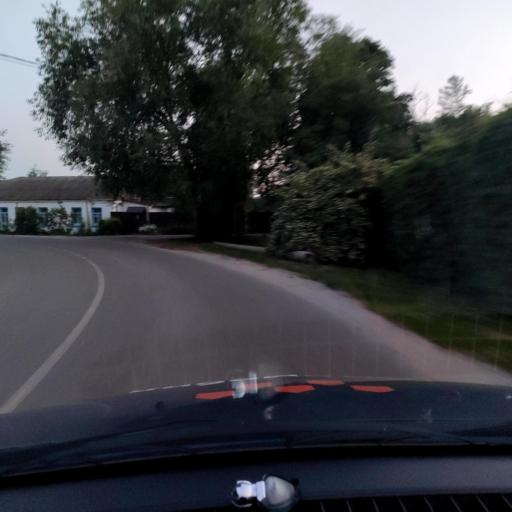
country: RU
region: Voronezj
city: Ramon'
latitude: 51.8204
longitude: 39.2659
